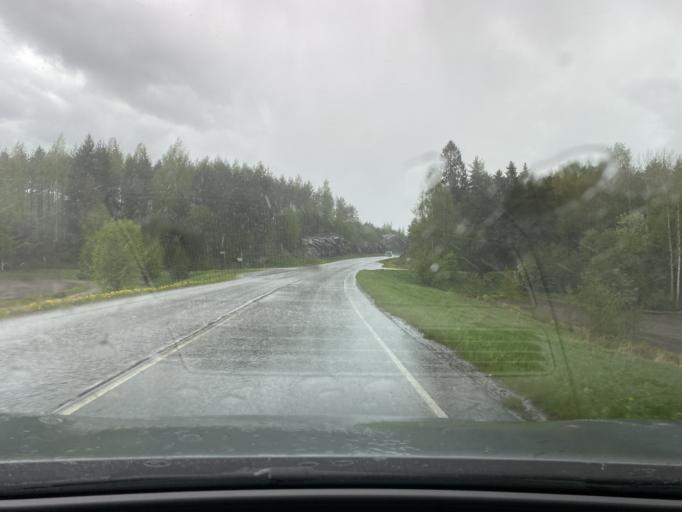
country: FI
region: Paijanne Tavastia
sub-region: Lahti
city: Jaervelae
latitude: 60.8081
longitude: 25.3642
